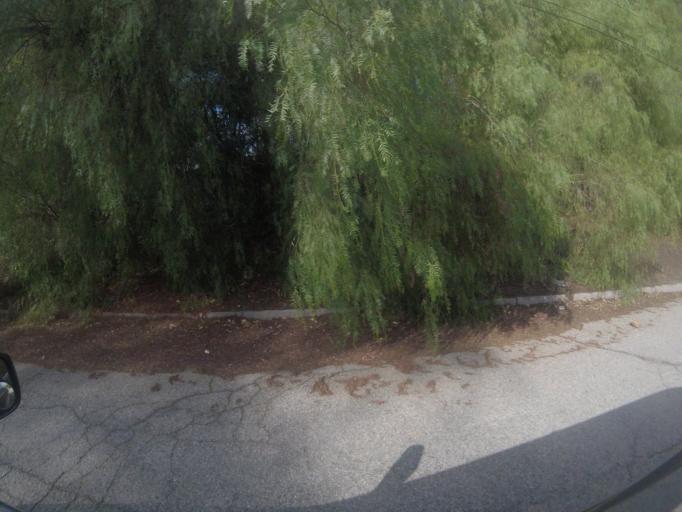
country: US
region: California
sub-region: San Bernardino County
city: Redlands
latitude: 34.0397
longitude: -117.1590
